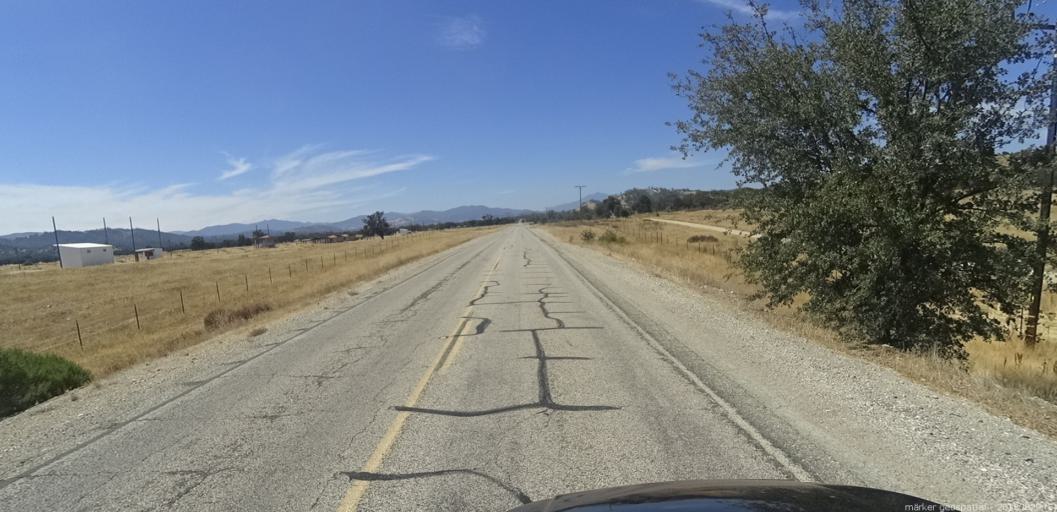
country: US
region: California
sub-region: Monterey County
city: King City
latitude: 35.9597
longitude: -121.1605
